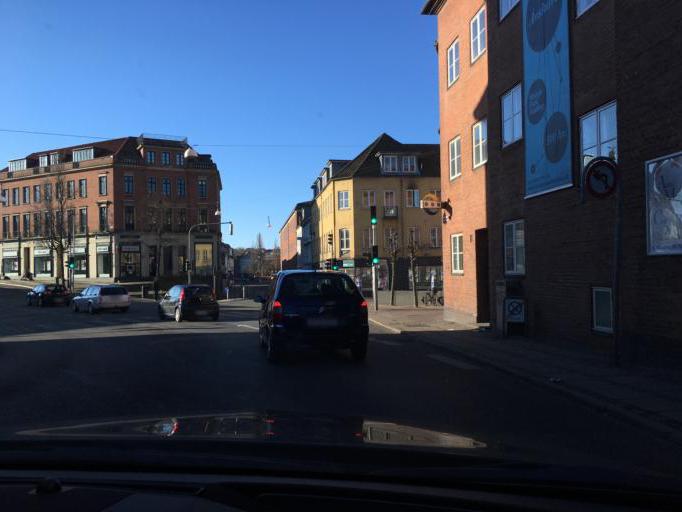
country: DK
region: South Denmark
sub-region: Kolding Kommune
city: Kolding
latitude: 55.4904
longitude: 9.4778
